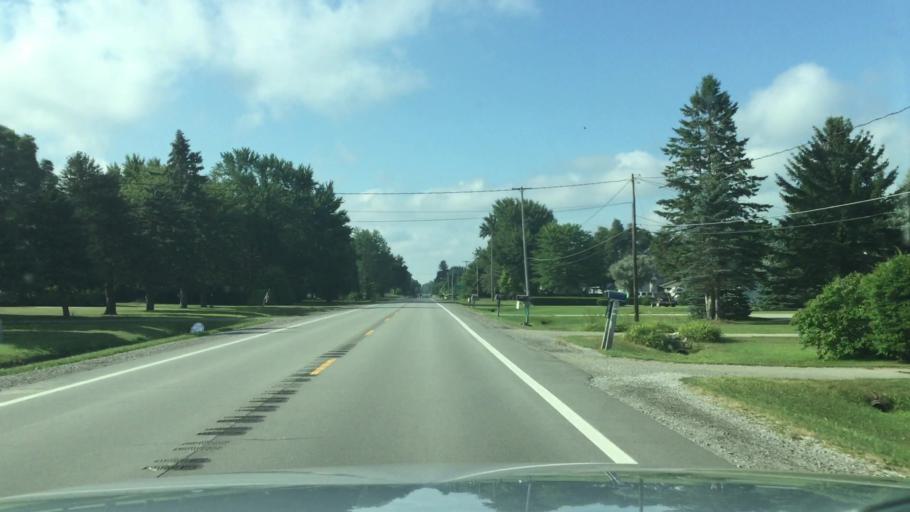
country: US
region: Michigan
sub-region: Saginaw County
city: Birch Run
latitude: 43.2395
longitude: -83.7353
